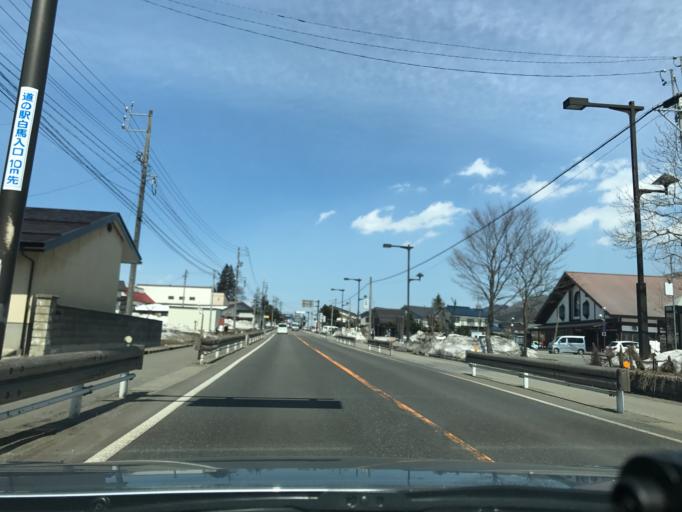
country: JP
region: Nagano
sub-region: Kitaazumi Gun
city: Hakuba
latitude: 36.6530
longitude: 137.8466
